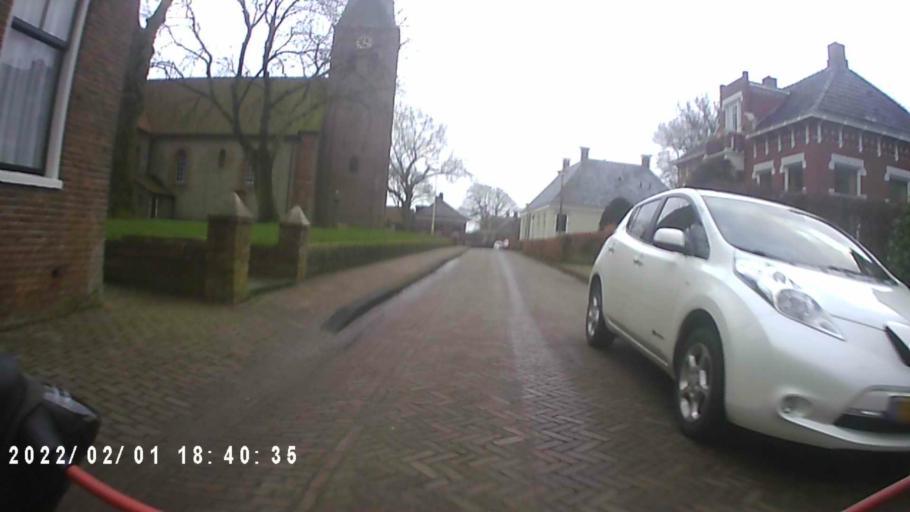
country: NL
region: Groningen
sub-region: Gemeente De Marne
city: Ulrum
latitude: 53.3600
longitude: 6.3738
